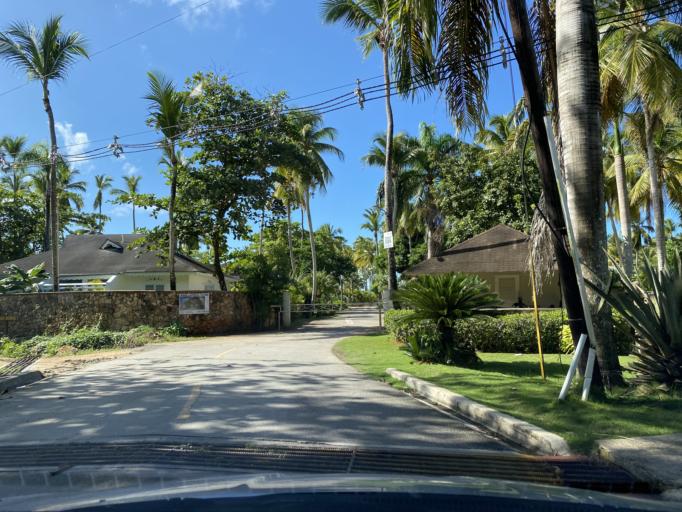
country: DO
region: Samana
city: Las Terrenas
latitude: 19.3128
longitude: -69.5727
